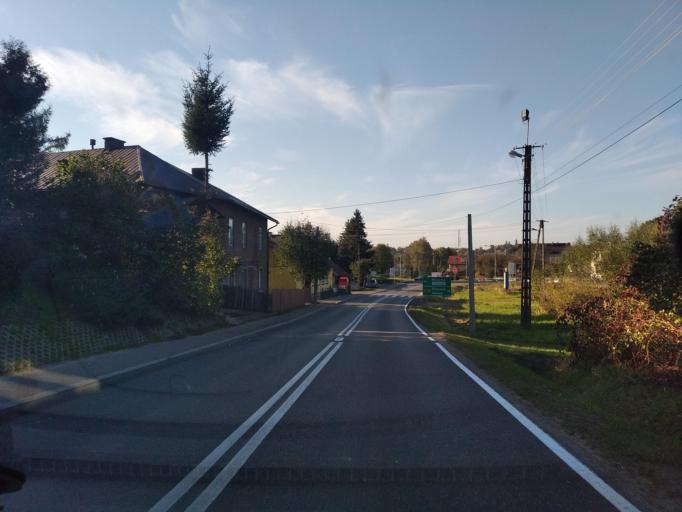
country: PL
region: Subcarpathian Voivodeship
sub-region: Powiat brzozowski
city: Brzozow
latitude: 49.6854
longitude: 22.0308
